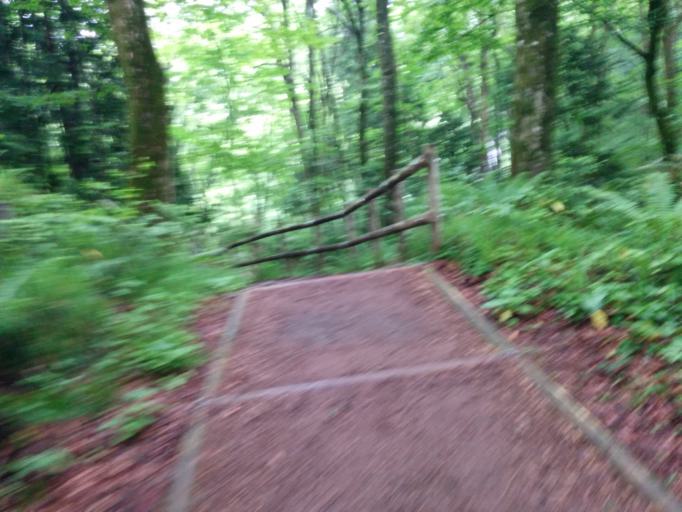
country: JP
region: Akita
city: Noshiromachi
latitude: 40.5643
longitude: 139.9794
